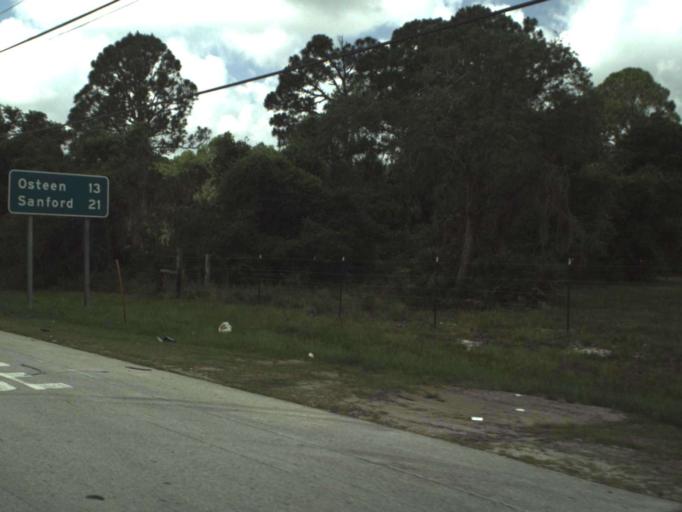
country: US
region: Florida
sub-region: Volusia County
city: Samsula-Spruce Creek
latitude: 29.0098
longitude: -81.0692
